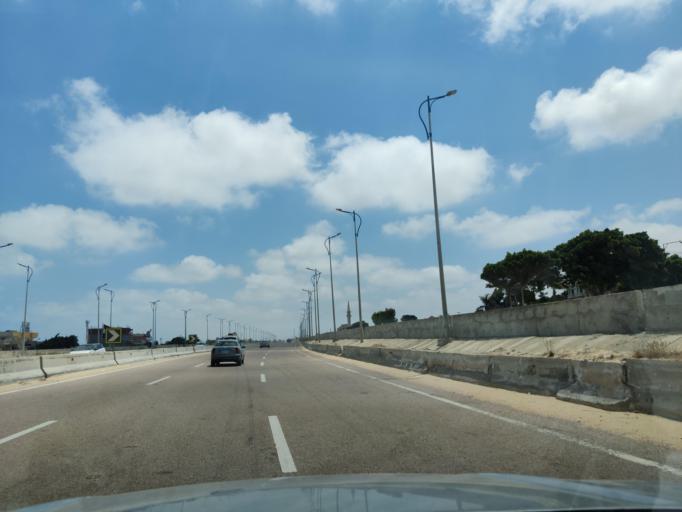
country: EG
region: Alexandria
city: Alexandria
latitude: 30.9585
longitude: 29.5387
